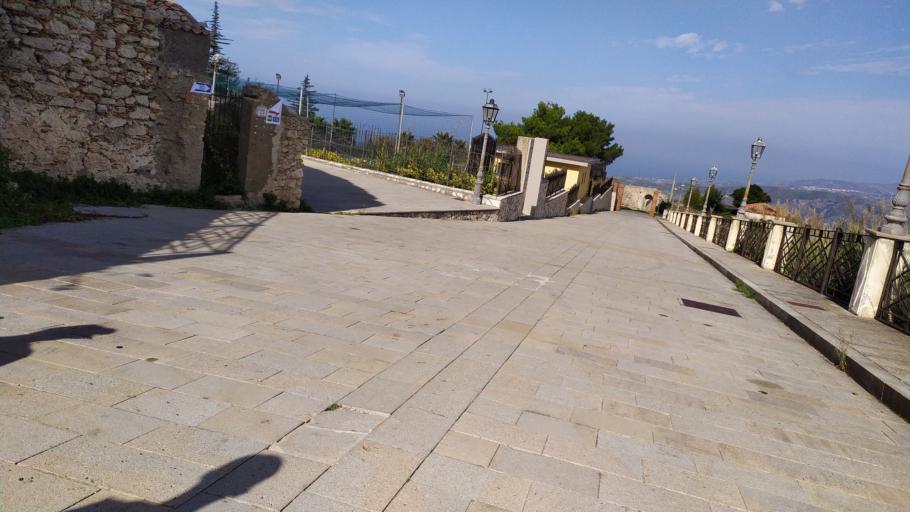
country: IT
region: Sicily
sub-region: Messina
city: Rometta
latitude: 38.1727
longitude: 15.4161
